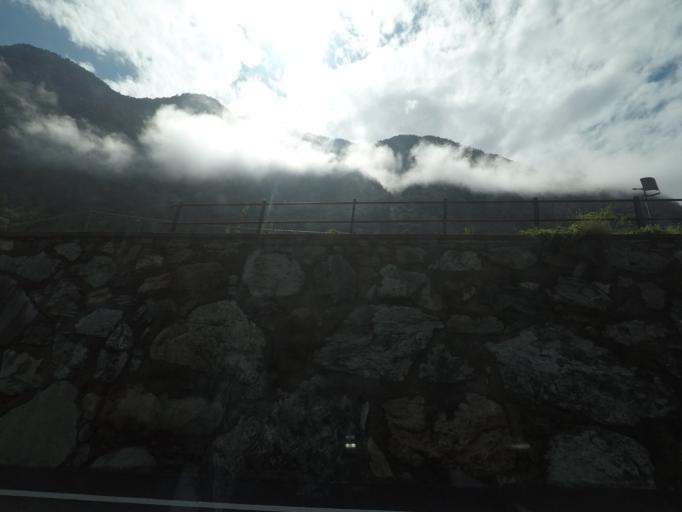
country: IT
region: Aosta Valley
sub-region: Valle d'Aosta
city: Antey-Saint-Andre
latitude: 45.7806
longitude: 7.5908
